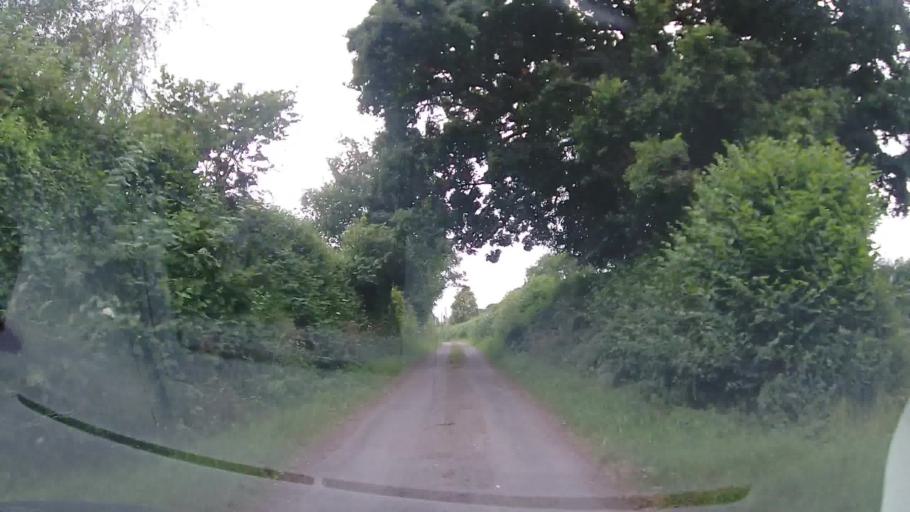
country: GB
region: England
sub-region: Shropshire
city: Prees
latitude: 52.9184
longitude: -2.6877
